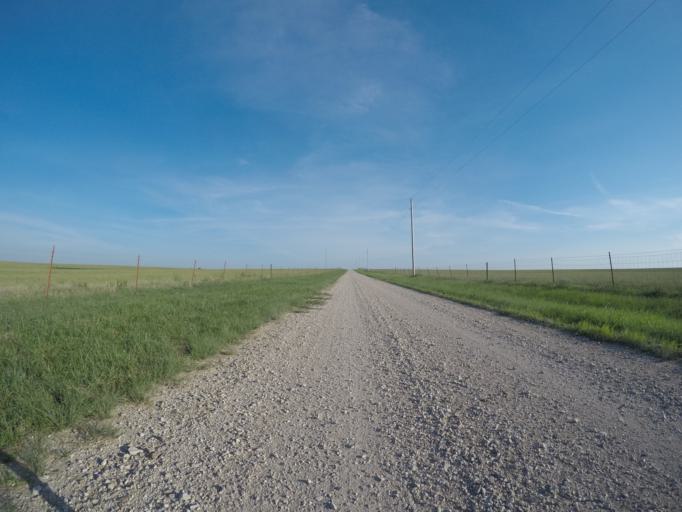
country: US
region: Kansas
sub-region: Riley County
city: Manhattan
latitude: 39.0135
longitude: -96.4919
